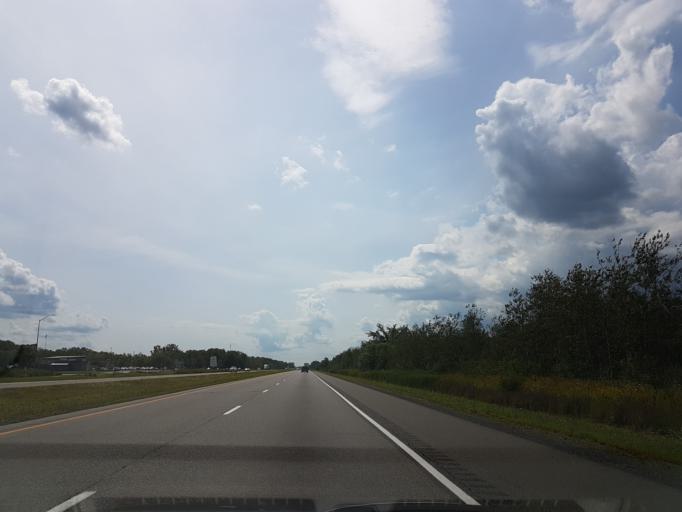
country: US
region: New York
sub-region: St. Lawrence County
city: Norfolk
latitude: 44.9467
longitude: -75.1267
